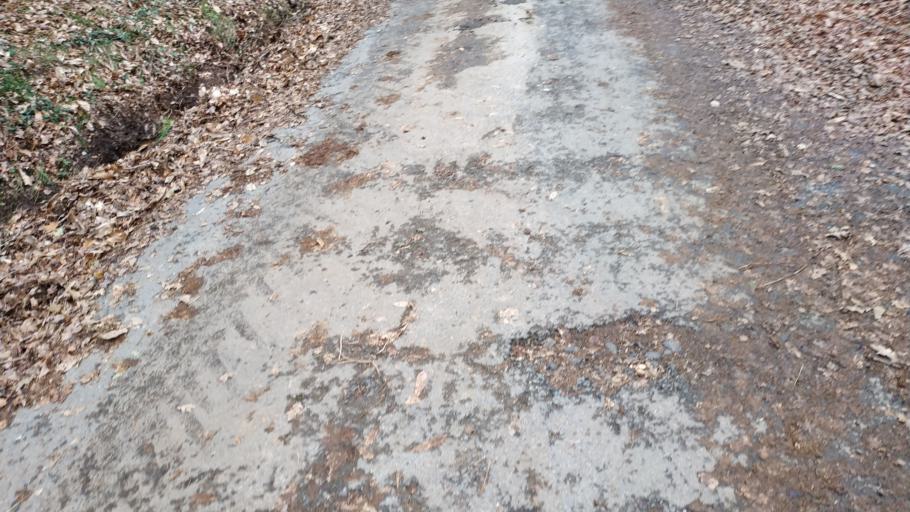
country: ES
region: Galicia
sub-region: Provincia de Pontevedra
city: Silleda
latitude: 42.7739
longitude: -8.1693
